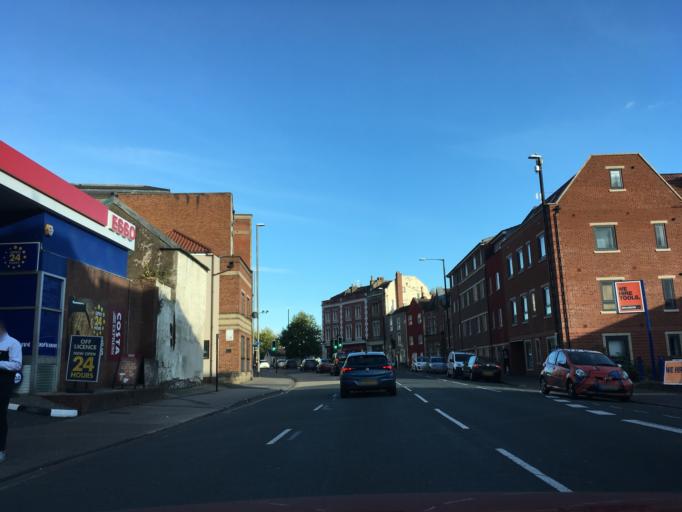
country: GB
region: England
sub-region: Bristol
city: Bristol
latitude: 51.4497
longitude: -2.6148
